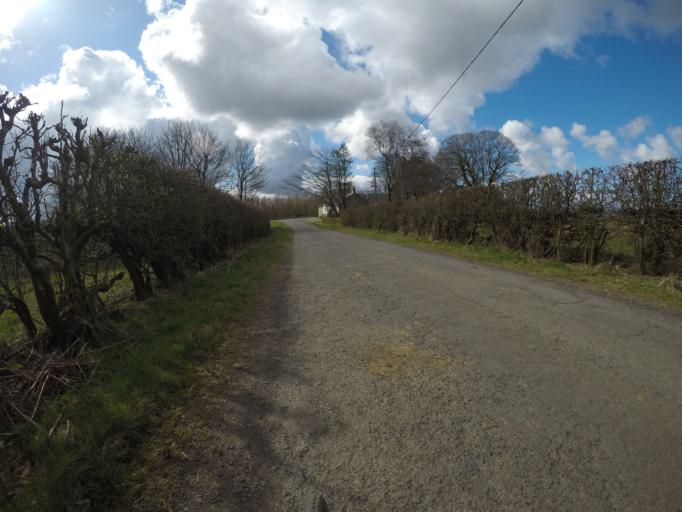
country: GB
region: Scotland
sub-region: North Ayrshire
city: Kilbirnie
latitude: 55.7219
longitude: -4.6671
